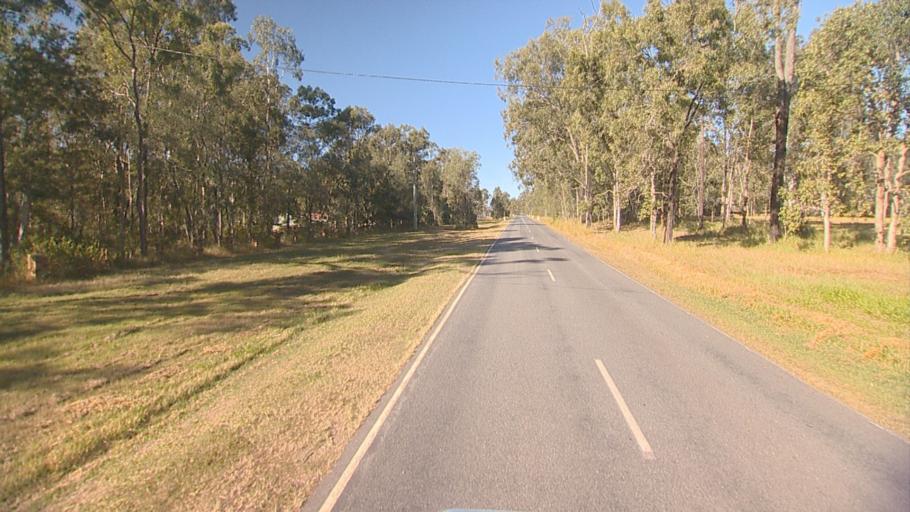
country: AU
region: Queensland
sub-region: Logan
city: North Maclean
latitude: -27.7908
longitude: 153.0338
